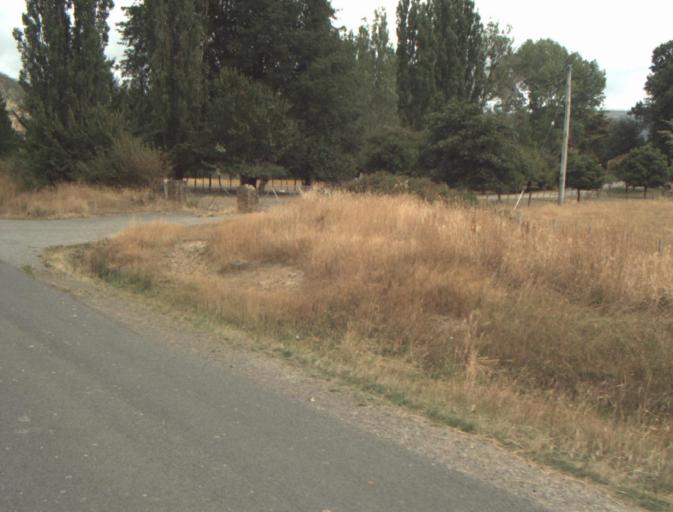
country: AU
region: Tasmania
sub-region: Northern Midlands
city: Evandale
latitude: -41.5044
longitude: 147.4825
